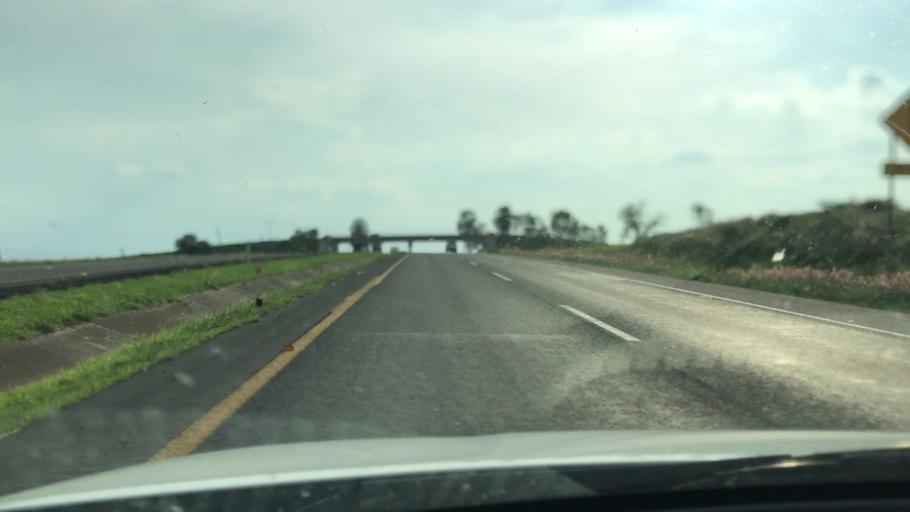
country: MX
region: Guanajuato
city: Penjamo
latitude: 20.3846
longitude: -101.7820
